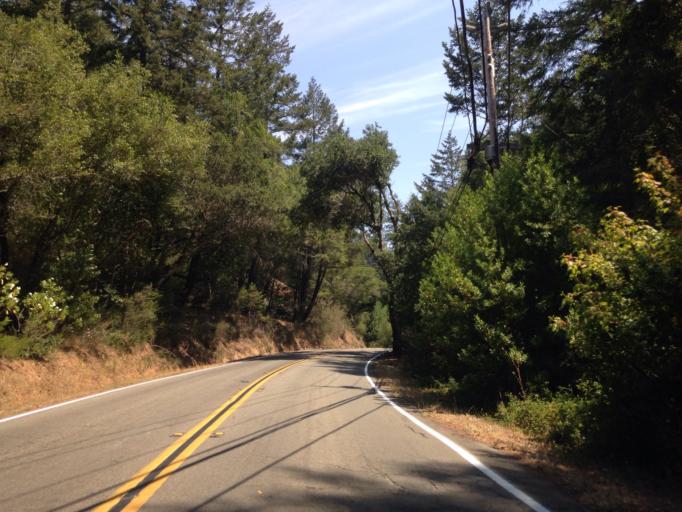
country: US
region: California
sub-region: Marin County
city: Lagunitas-Forest Knolls
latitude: 38.0504
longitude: -122.6732
